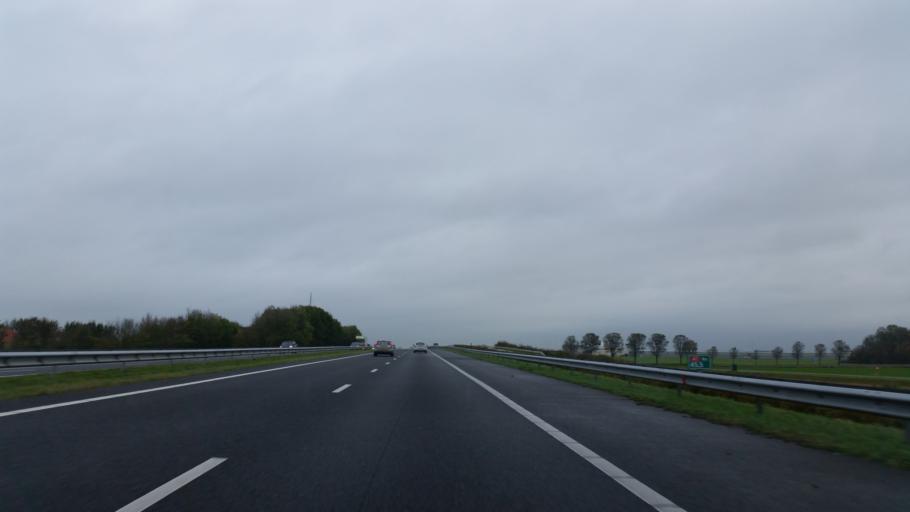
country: NL
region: North Holland
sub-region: Gemeente Medemblik
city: Opperdoes
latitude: 52.7703
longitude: 5.0345
